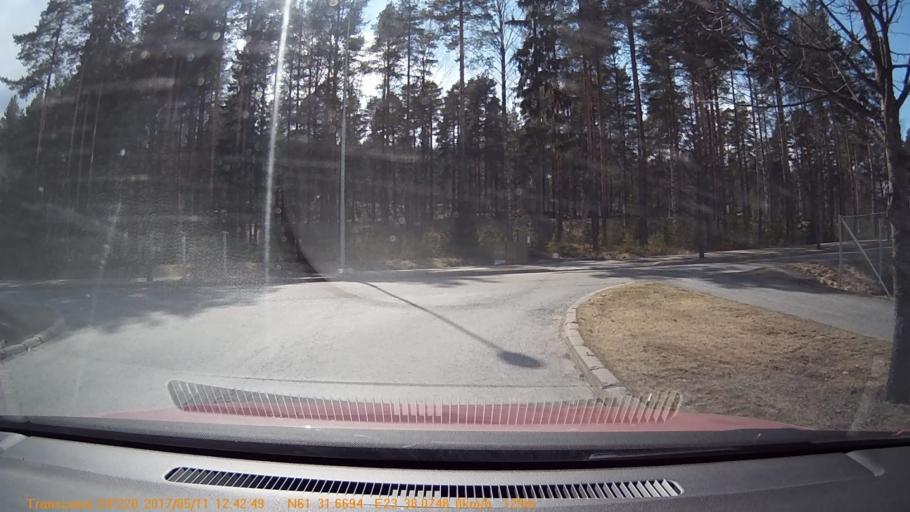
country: FI
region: Pirkanmaa
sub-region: Tampere
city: Yloejaervi
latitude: 61.5278
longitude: 23.6346
